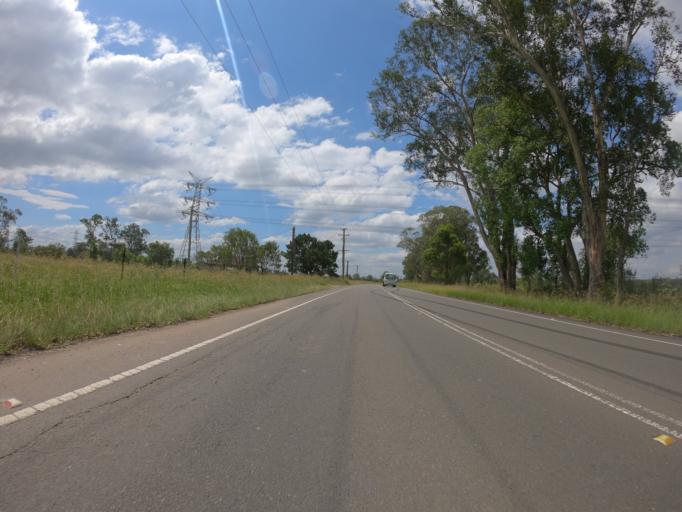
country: AU
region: New South Wales
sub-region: Penrith Municipality
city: Kingswood Park
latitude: -33.8127
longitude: 150.7603
